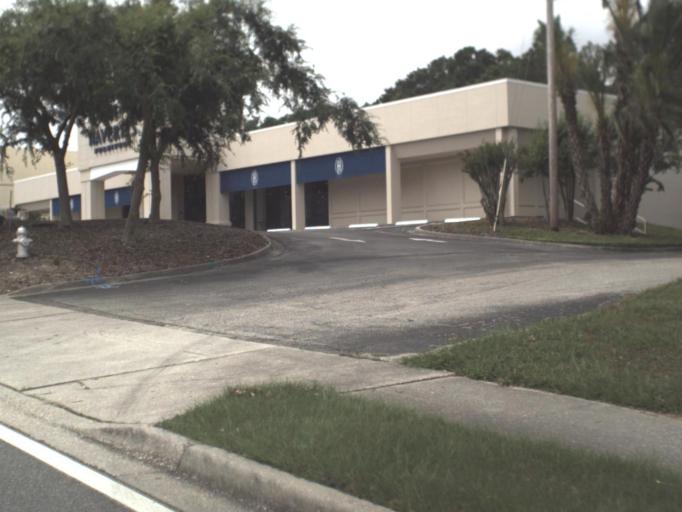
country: US
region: Florida
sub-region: Clay County
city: Bellair-Meadowbrook Terrace
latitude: 30.1839
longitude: -81.7395
